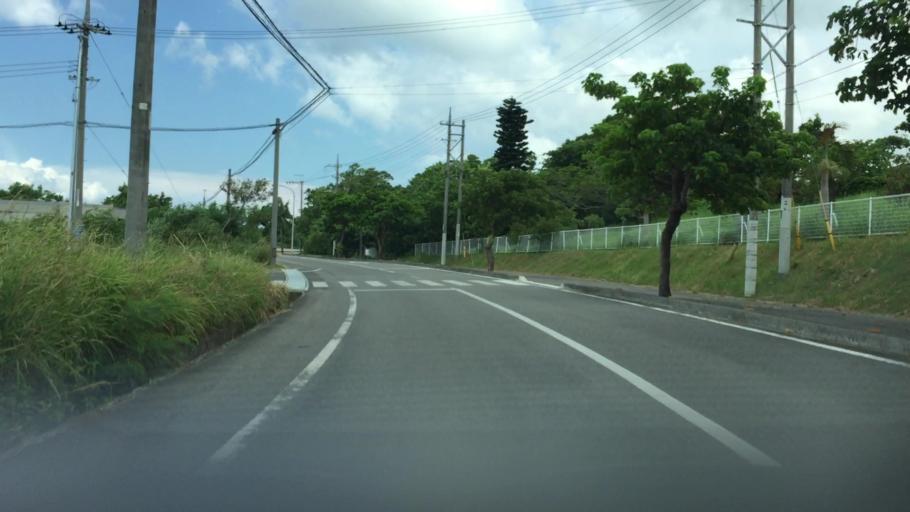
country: JP
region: Okinawa
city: Ishigaki
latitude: 24.3646
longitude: 124.1414
